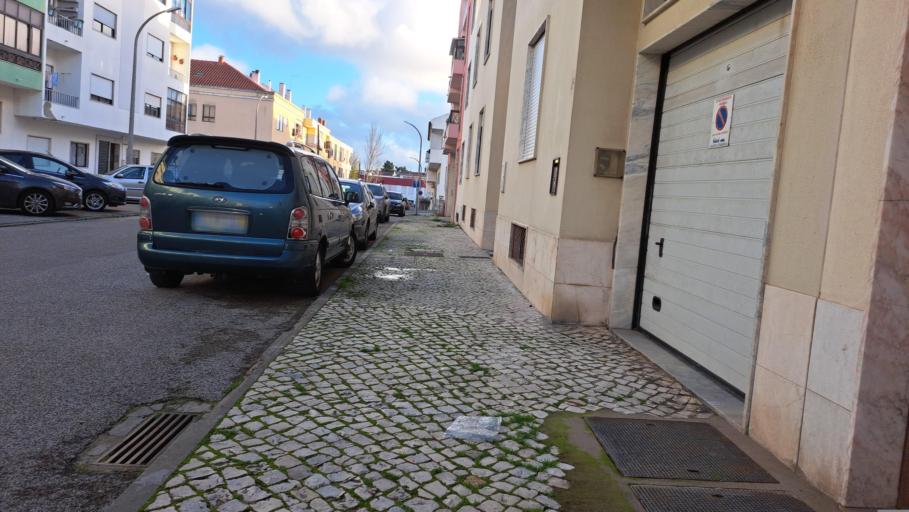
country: PT
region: Setubal
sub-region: Moita
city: Alhos Vedros
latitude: 38.6516
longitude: -9.0454
